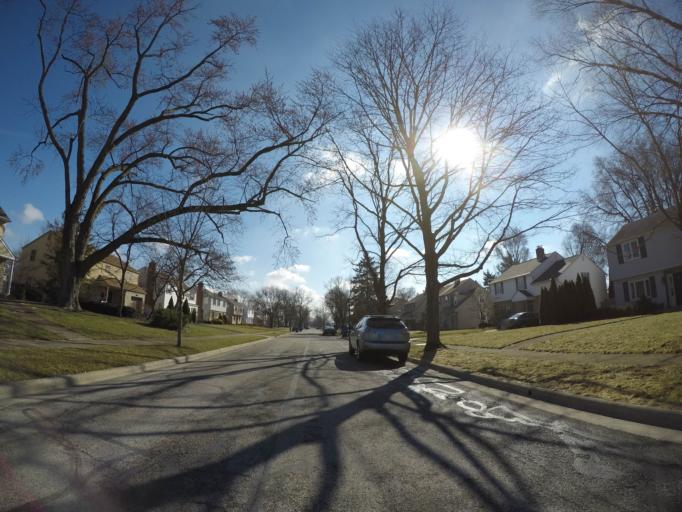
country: US
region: Ohio
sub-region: Franklin County
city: Upper Arlington
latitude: 40.0034
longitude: -83.0514
